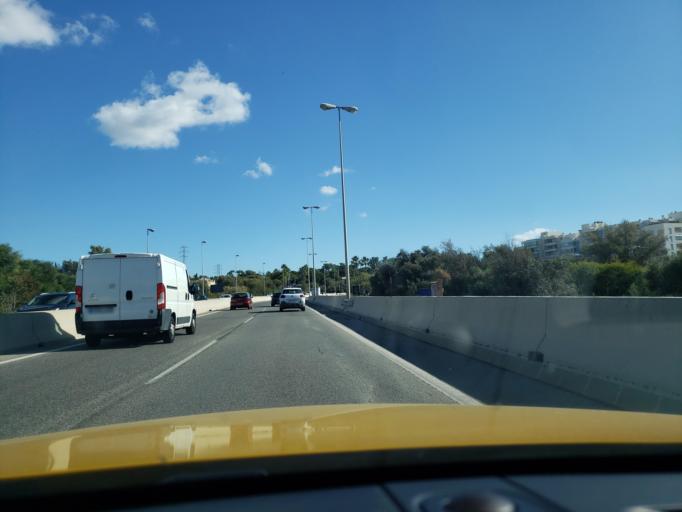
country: ES
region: Andalusia
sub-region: Provincia de Malaga
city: Marbella
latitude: 36.5053
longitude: -4.8142
